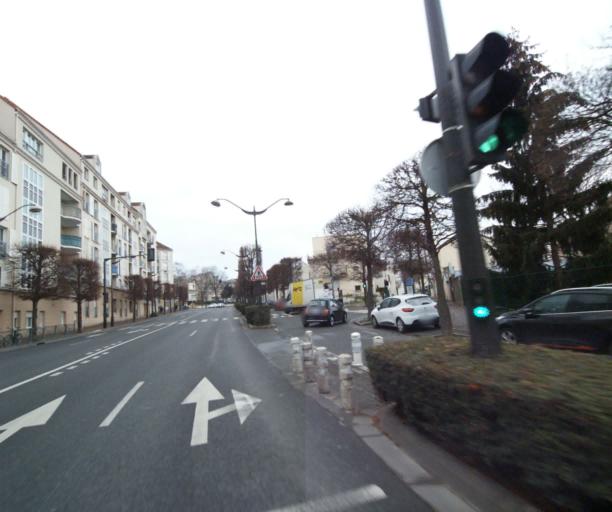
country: FR
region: Ile-de-France
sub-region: Departement des Hauts-de-Seine
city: Rueil-Malmaison
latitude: 48.8780
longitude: 2.1868
